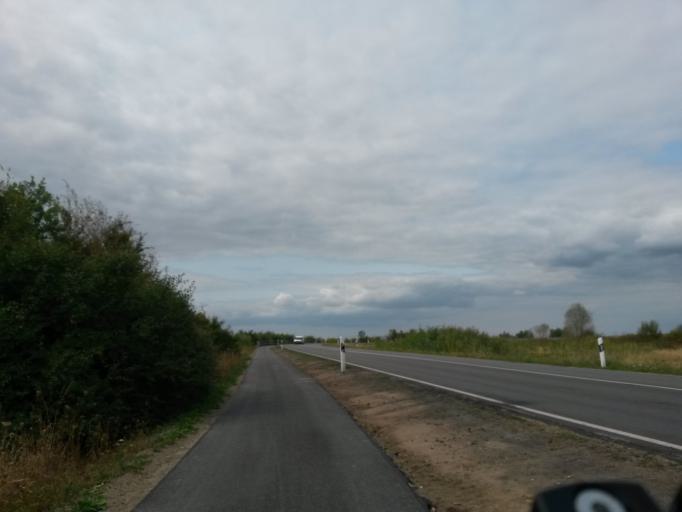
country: DE
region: Saxony-Anhalt
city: Schonhausen
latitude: 52.5498
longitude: 12.0220
